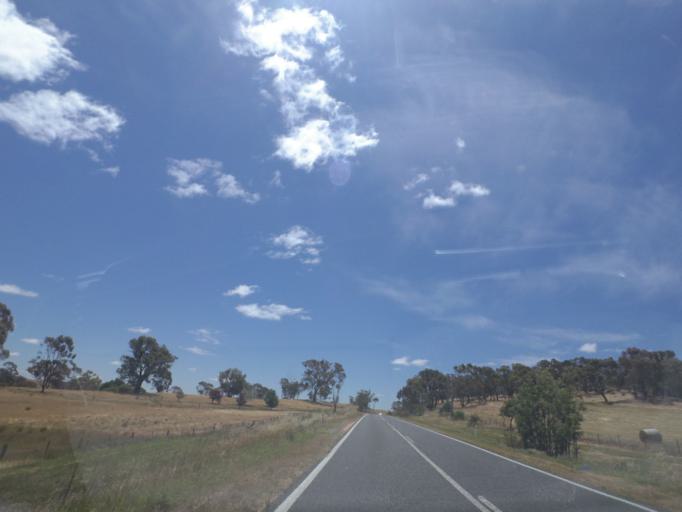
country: AU
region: Victoria
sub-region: Mount Alexander
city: Castlemaine
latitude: -37.2163
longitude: 144.1405
